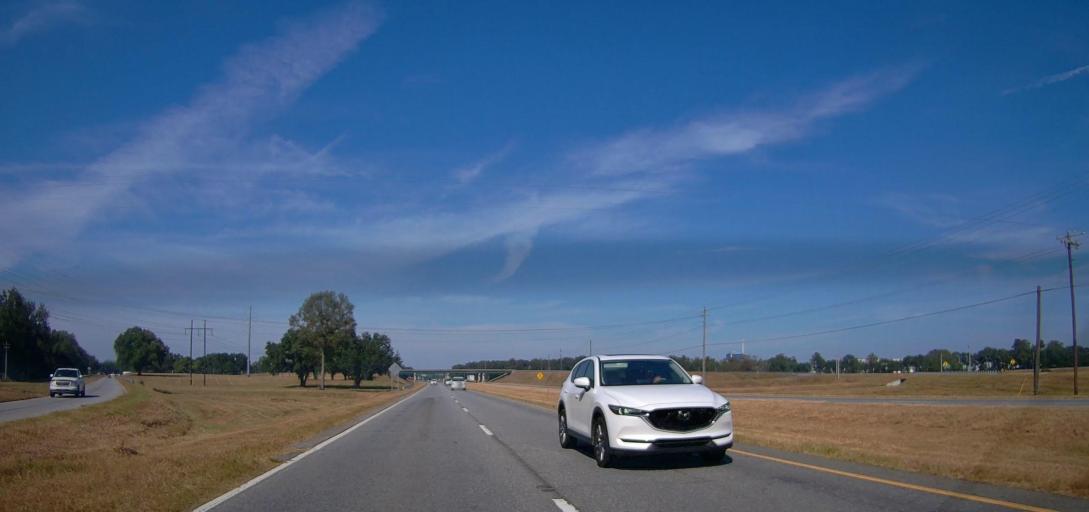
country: US
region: Georgia
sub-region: Dougherty County
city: Albany
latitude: 31.5421
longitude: -84.1152
